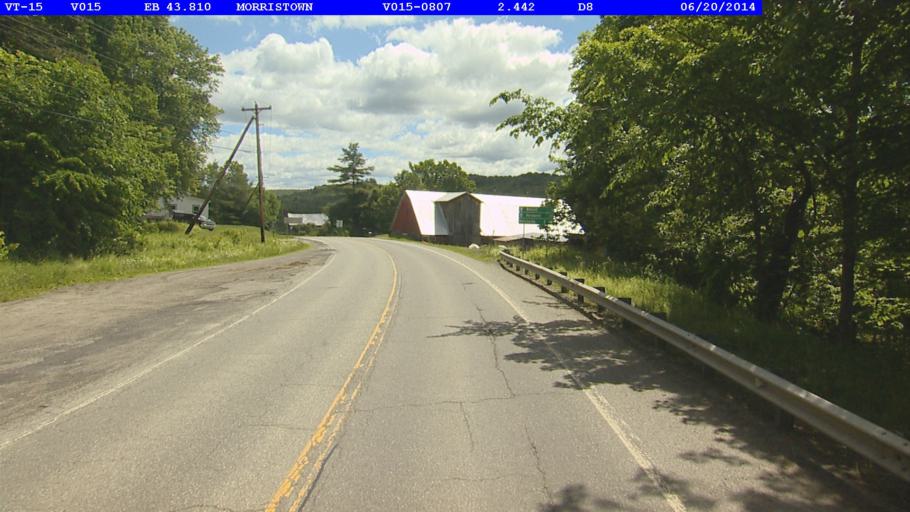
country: US
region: Vermont
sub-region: Lamoille County
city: Morrisville
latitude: 44.5661
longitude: -72.5659
